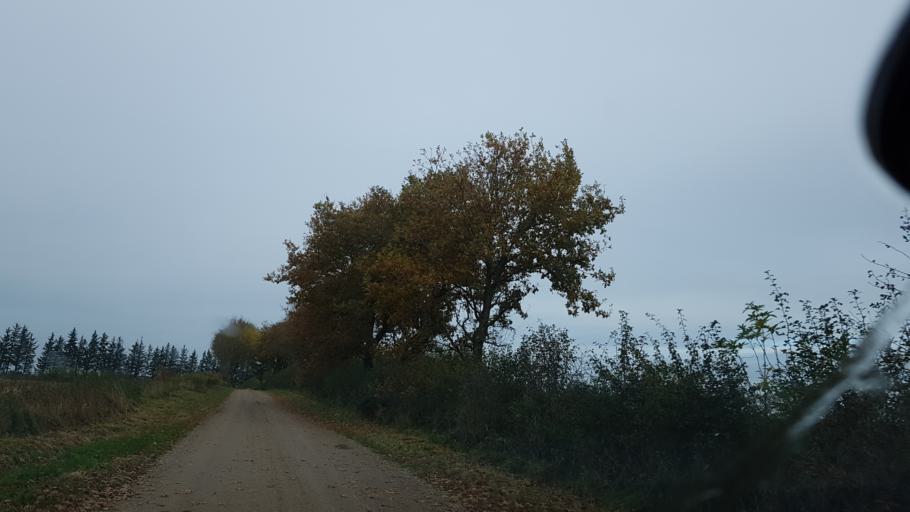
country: DK
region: South Denmark
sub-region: Tonder Kommune
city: Sherrebek
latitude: 55.2234
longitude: 8.8686
